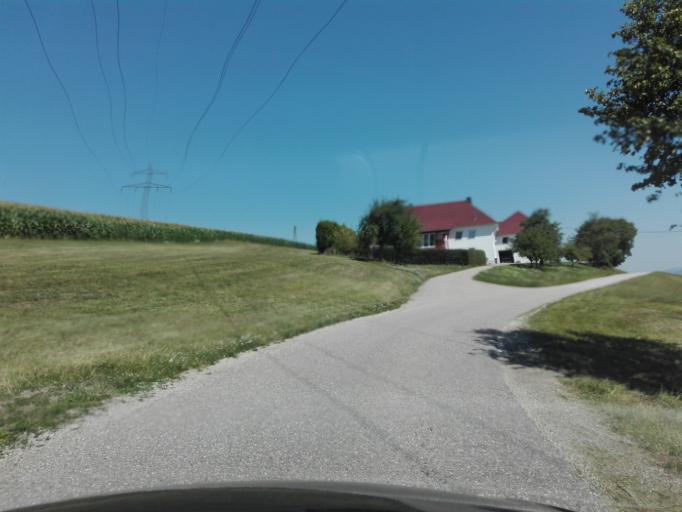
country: AT
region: Upper Austria
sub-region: Politischer Bezirk Urfahr-Umgebung
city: Steyregg
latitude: 48.3058
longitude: 14.3775
